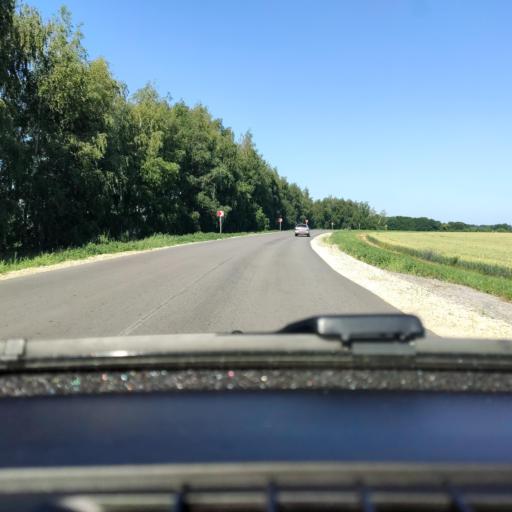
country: RU
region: Voronezj
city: Pereleshinskiy
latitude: 51.6441
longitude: 40.2916
